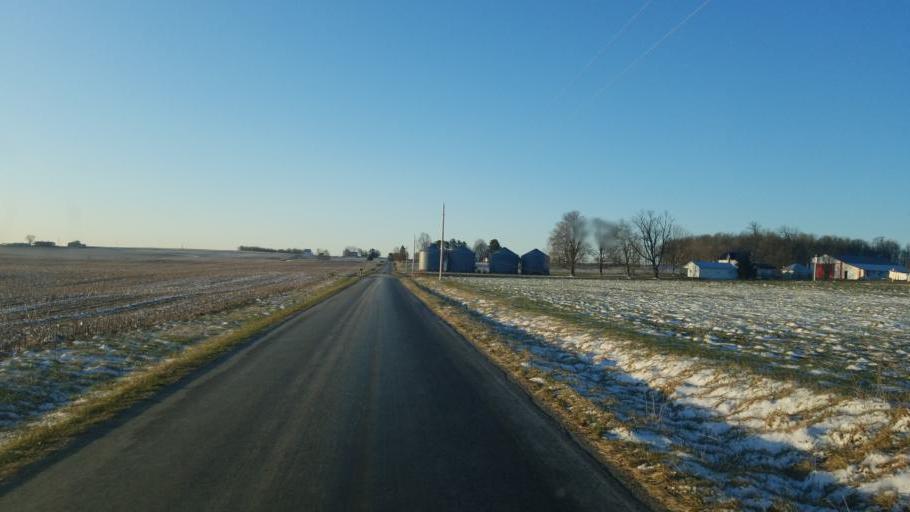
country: US
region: Ohio
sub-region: Highland County
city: Leesburg
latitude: 39.2502
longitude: -83.5011
